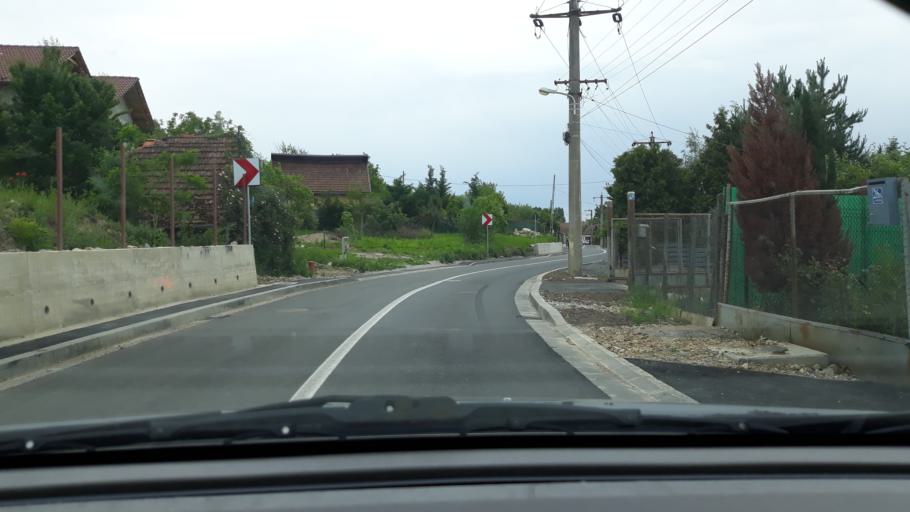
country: RO
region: Bihor
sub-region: Comuna Osorheiu
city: Alparea
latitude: 47.0599
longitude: 22.0064
